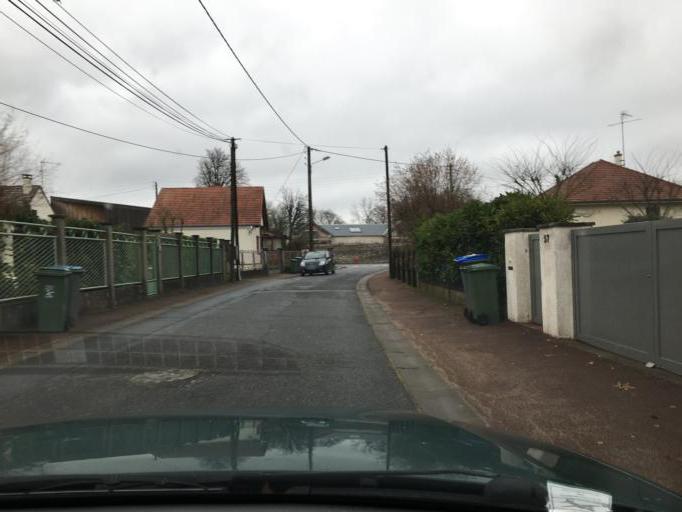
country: FR
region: Centre
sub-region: Departement du Loiret
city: Saint-Pryve-Saint-Mesmin
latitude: 47.8670
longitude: 1.8767
